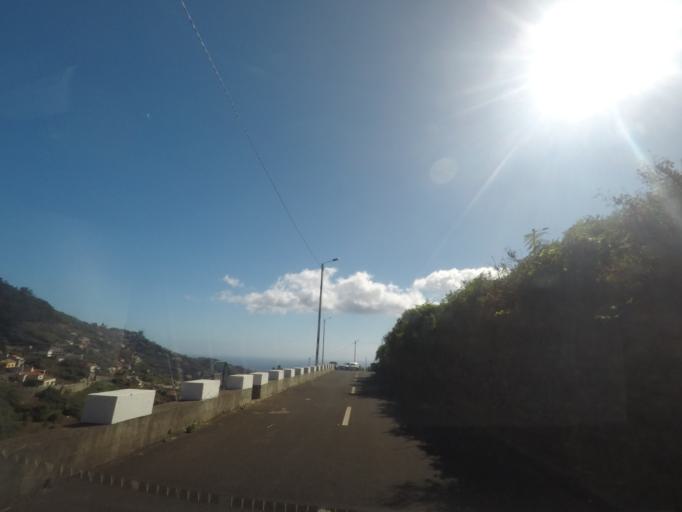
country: PT
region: Madeira
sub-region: Ribeira Brava
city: Campanario
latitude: 32.6772
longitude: -17.0232
